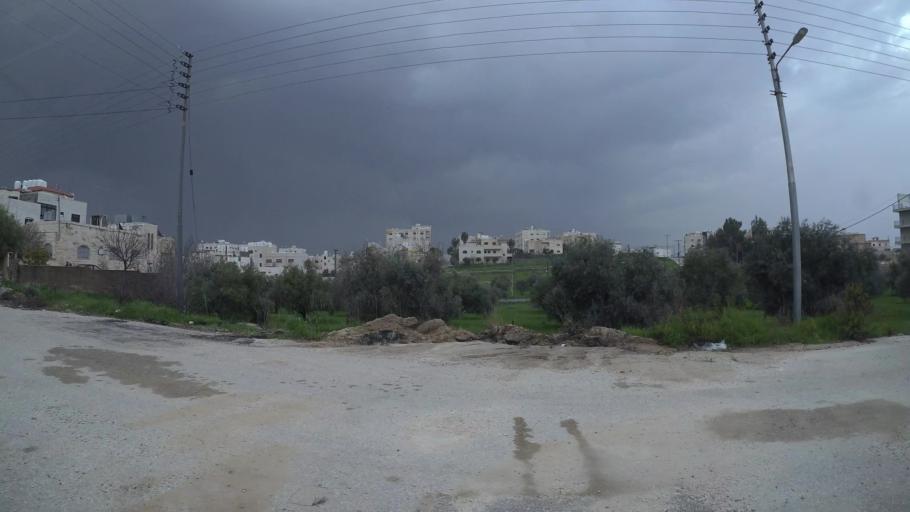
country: JO
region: Amman
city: Umm as Summaq
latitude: 31.8851
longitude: 35.8596
